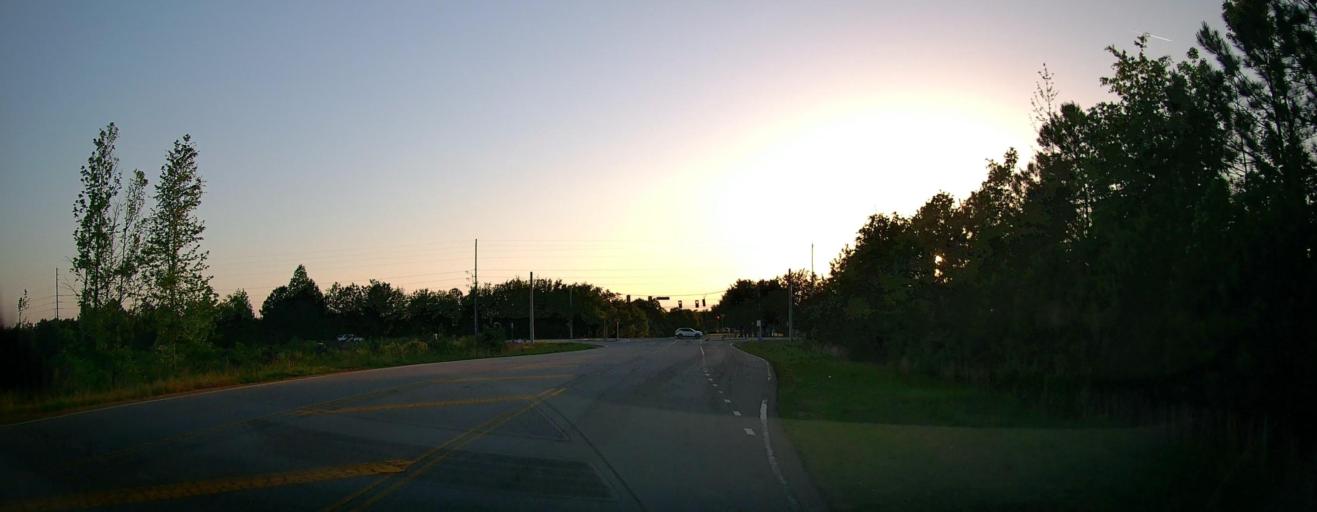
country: US
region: Georgia
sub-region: Henry County
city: McDonough
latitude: 33.4026
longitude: -84.1384
